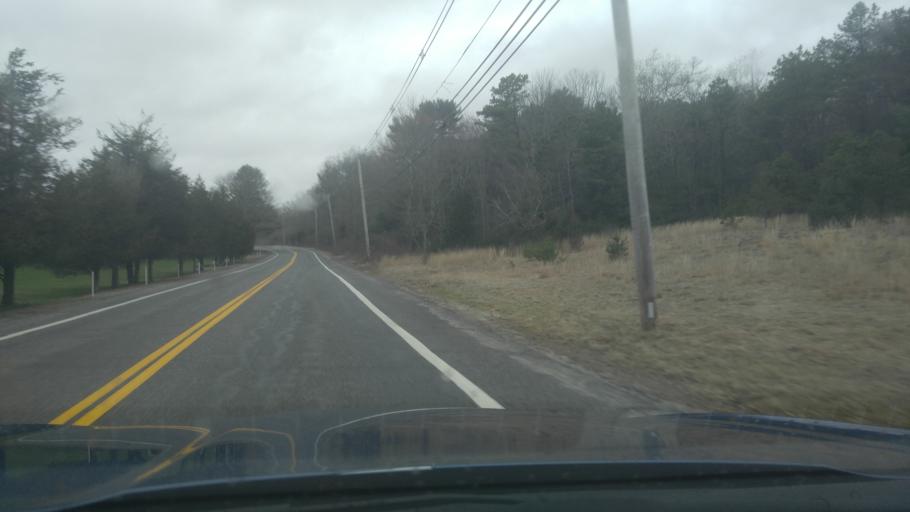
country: US
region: Rhode Island
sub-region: Kent County
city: West Greenwich
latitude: 41.6718
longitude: -71.6314
